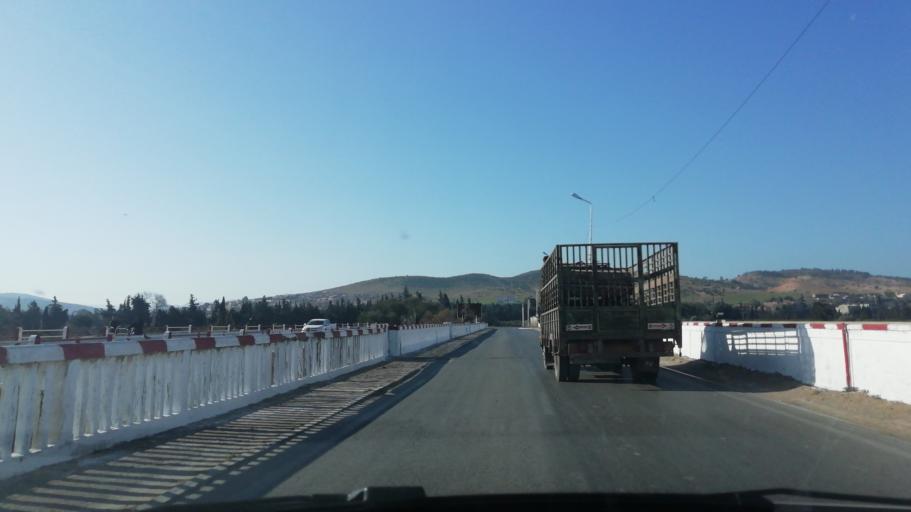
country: DZ
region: Mascara
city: Mascara
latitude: 35.5870
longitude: 0.0530
